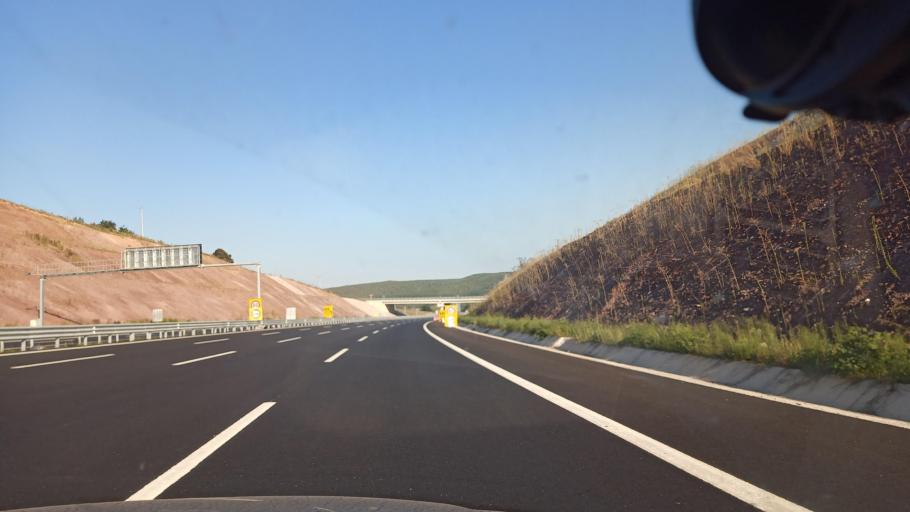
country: TR
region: Sakarya
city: Adapazari
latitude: 40.8389
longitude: 30.3782
